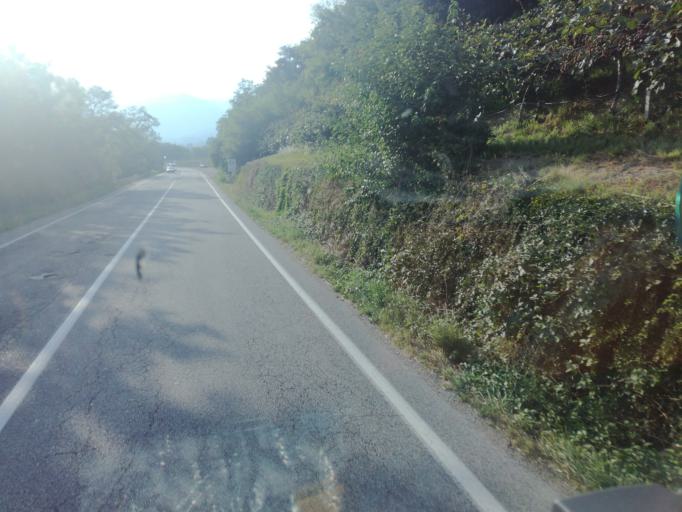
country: IT
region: Piedmont
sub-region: Provincia di Torino
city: Bibiana
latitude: 44.8090
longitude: 7.2861
